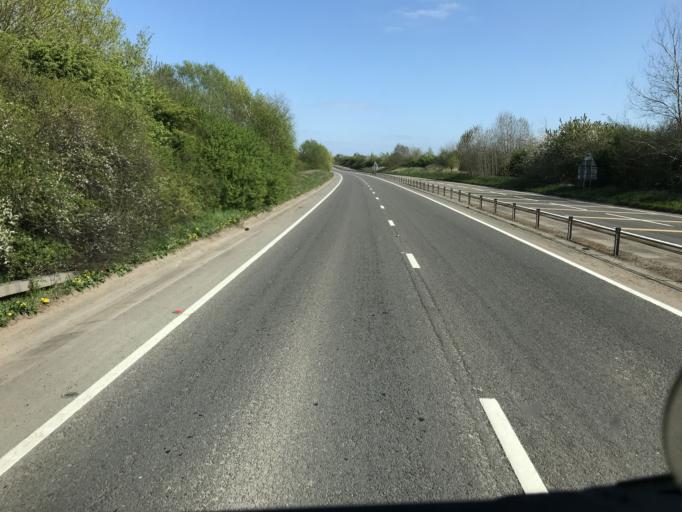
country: GB
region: England
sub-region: Cheshire East
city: Crewe
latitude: 53.0705
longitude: -2.4341
